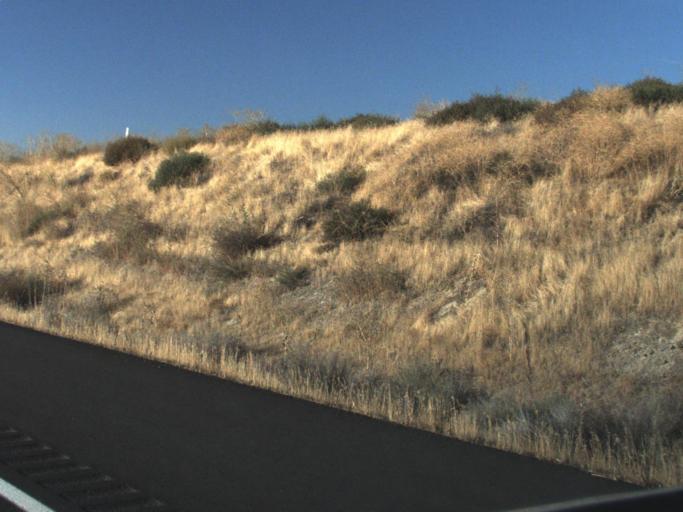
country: US
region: Washington
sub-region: Franklin County
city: Connell
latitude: 46.7098
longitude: -118.8364
